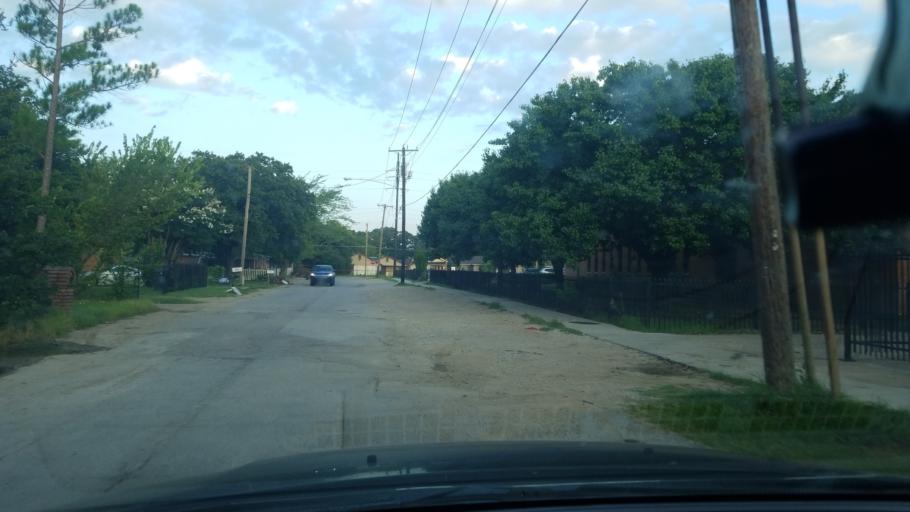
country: US
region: Texas
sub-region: Dallas County
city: Balch Springs
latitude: 32.7299
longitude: -96.6556
